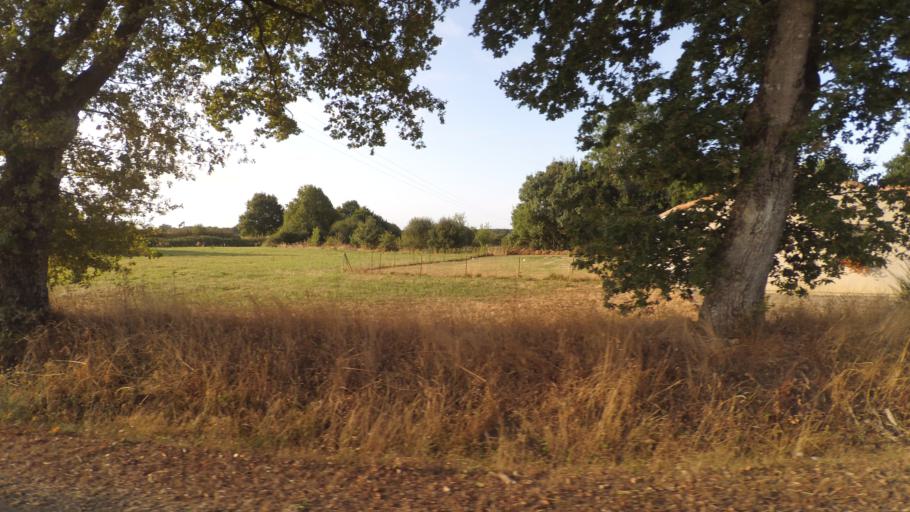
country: FR
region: Pays de la Loire
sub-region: Departement de la Loire-Atlantique
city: Vieillevigne
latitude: 46.9871
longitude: -1.4595
